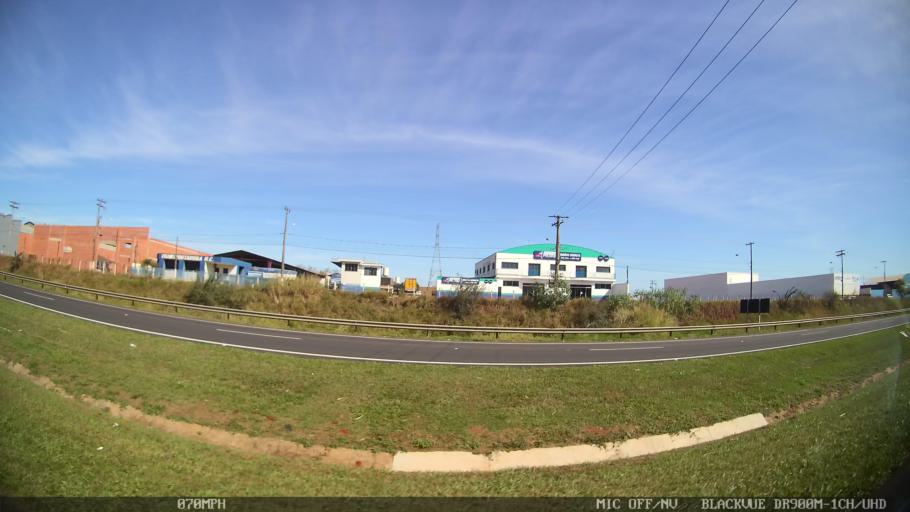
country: BR
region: Sao Paulo
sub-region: Porto Ferreira
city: Porto Ferreira
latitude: -21.8728
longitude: -47.4885
